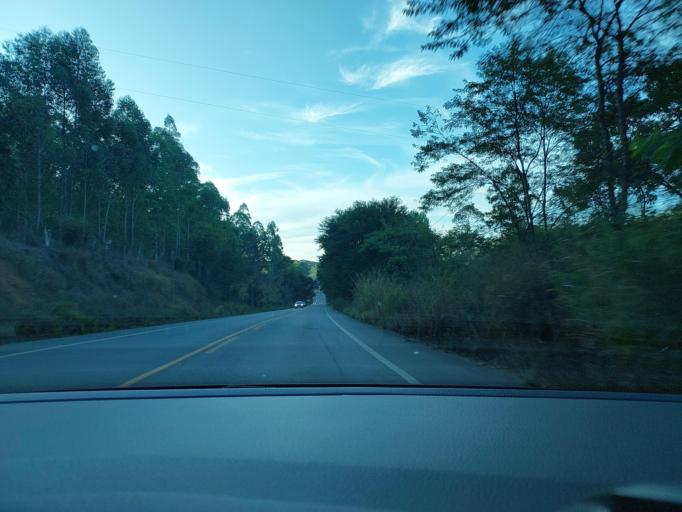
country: BR
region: Minas Gerais
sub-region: Vicosa
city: Vicosa
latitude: -20.8338
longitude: -42.8129
